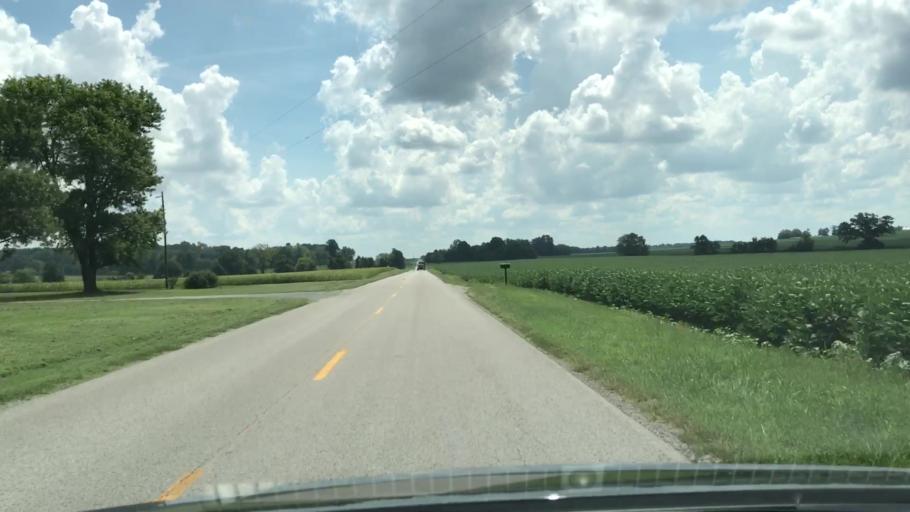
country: US
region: Kentucky
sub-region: Todd County
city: Guthrie
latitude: 36.7056
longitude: -87.0454
